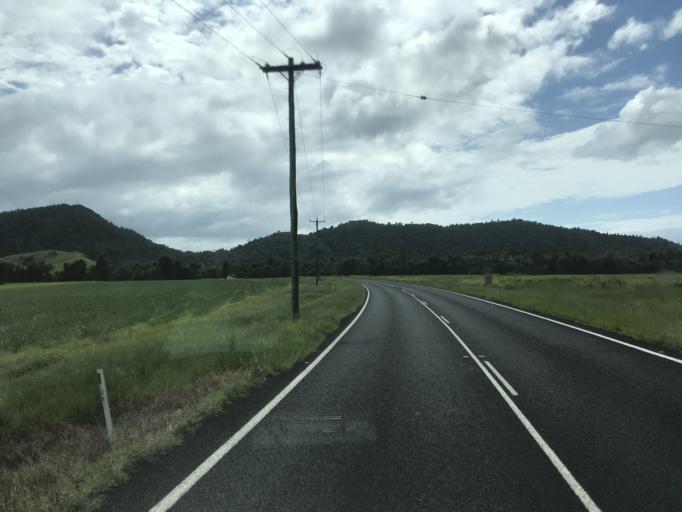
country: AU
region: Queensland
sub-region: Cassowary Coast
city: Innisfail
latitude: -17.8245
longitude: 146.0463
